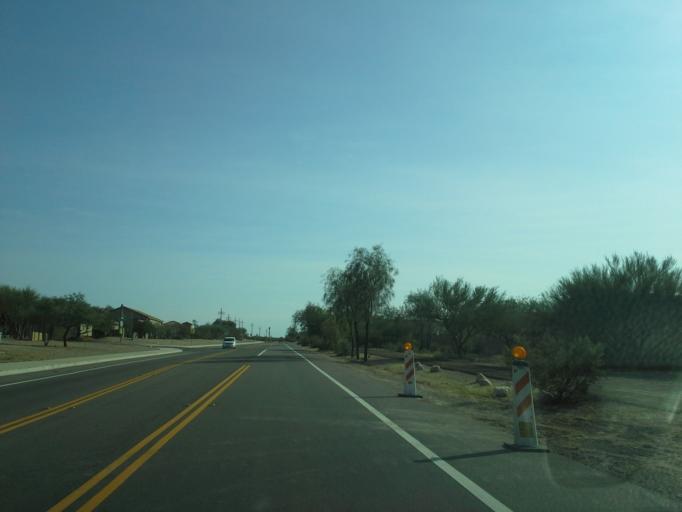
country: US
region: Arizona
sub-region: Pima County
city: Flowing Wells
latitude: 32.2438
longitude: -111.0205
